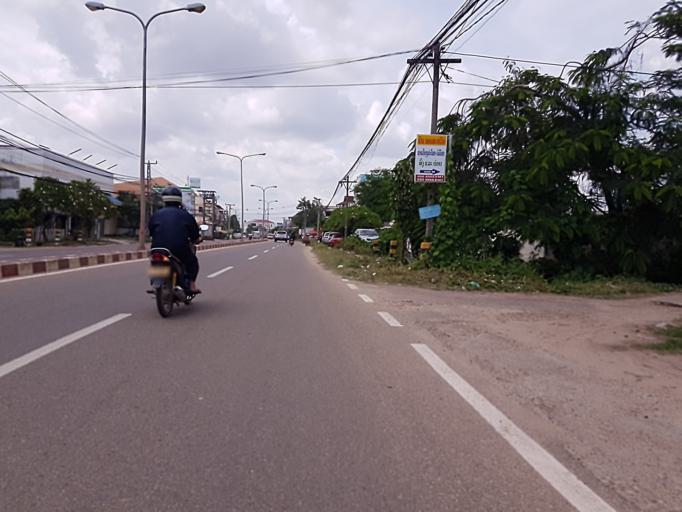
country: TH
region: Nong Khai
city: Si Chiang Mai
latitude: 17.9163
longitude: 102.6198
